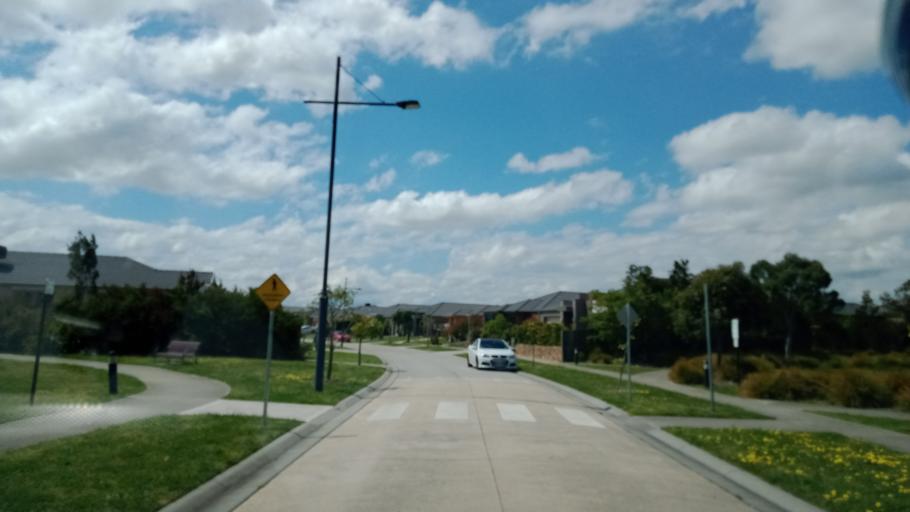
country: AU
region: Victoria
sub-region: Frankston
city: Sandhurst
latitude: -38.0833
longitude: 145.1951
